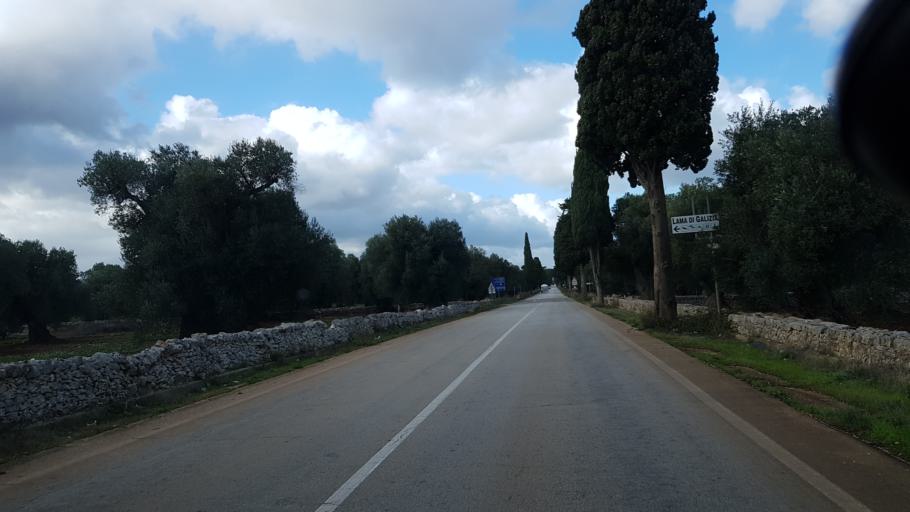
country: IT
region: Apulia
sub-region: Provincia di Brindisi
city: Montalbano
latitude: 40.7659
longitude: 17.5169
